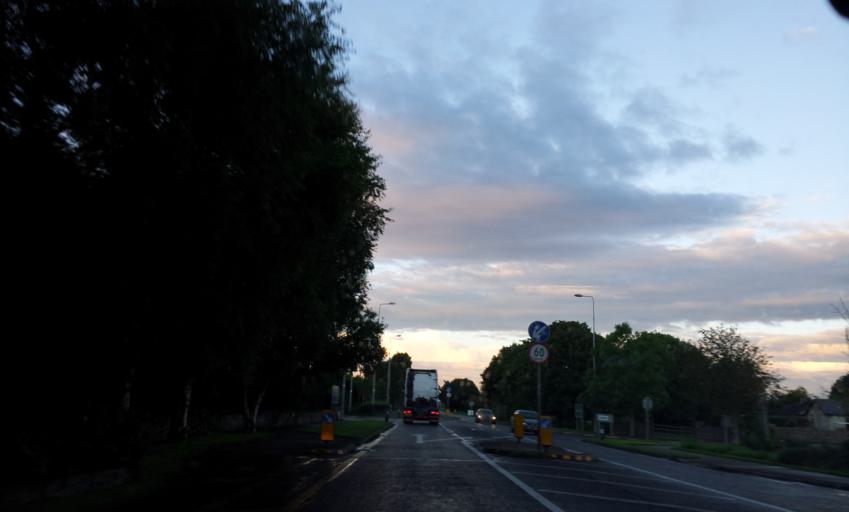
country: IE
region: Munster
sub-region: County Limerick
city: Rathkeale
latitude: 52.5338
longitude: -8.8712
